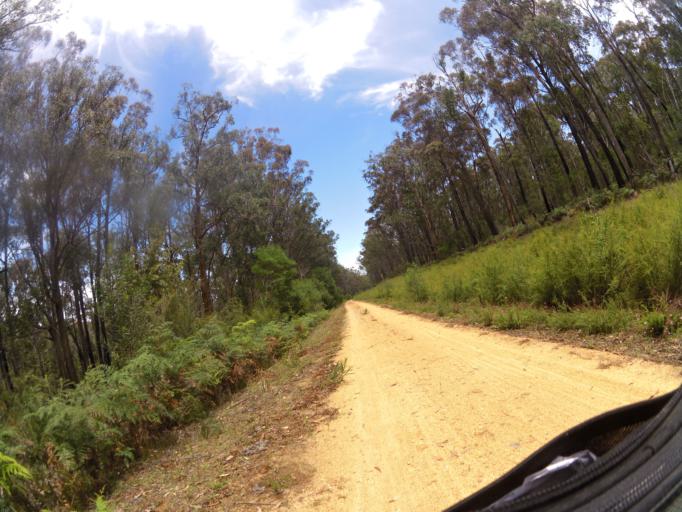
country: AU
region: Victoria
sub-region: East Gippsland
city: Lakes Entrance
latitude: -37.7413
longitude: 148.0033
